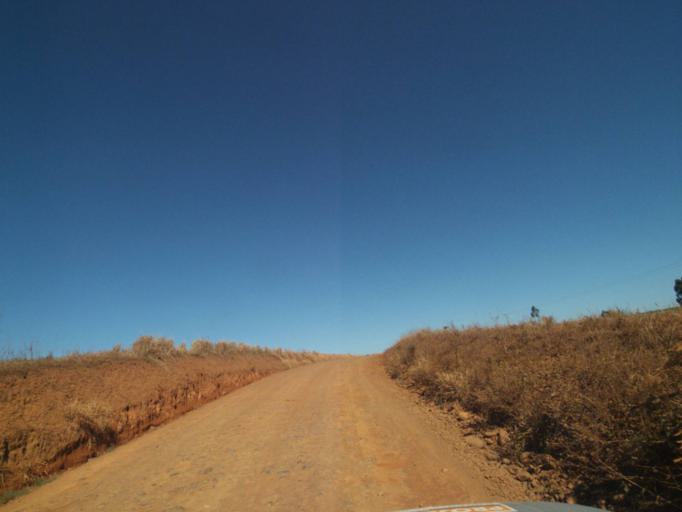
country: BR
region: Parana
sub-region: Tibagi
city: Tibagi
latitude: -24.5979
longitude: -50.6023
